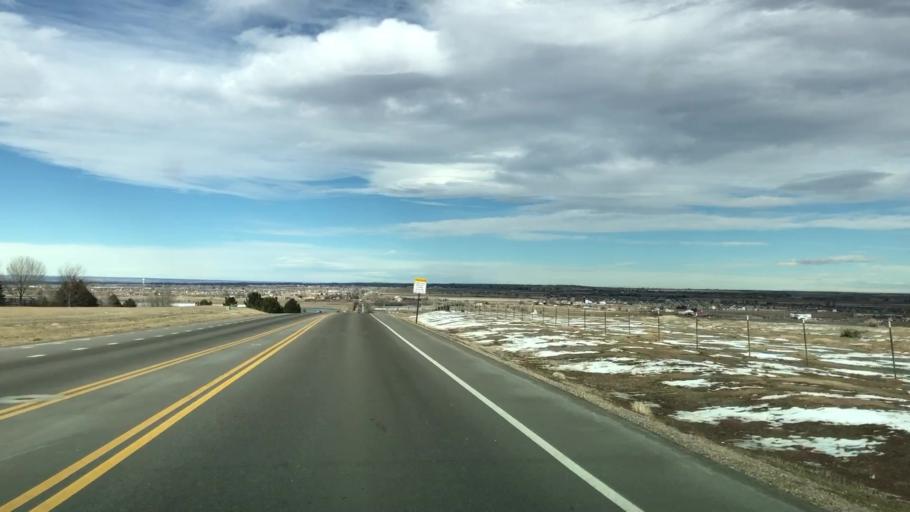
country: US
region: Colorado
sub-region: Weld County
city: Windsor
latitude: 40.4650
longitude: -104.9441
